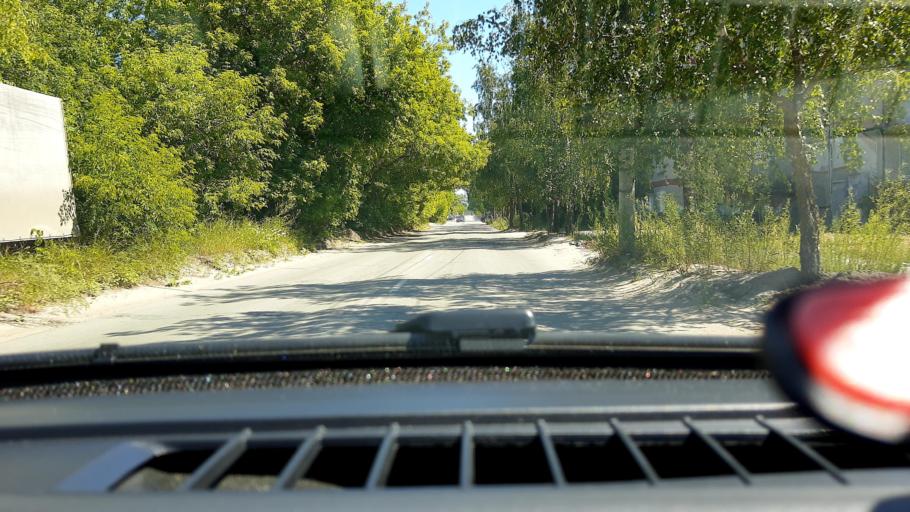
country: RU
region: Nizjnij Novgorod
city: Dzerzhinsk
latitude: 56.2549
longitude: 43.4723
